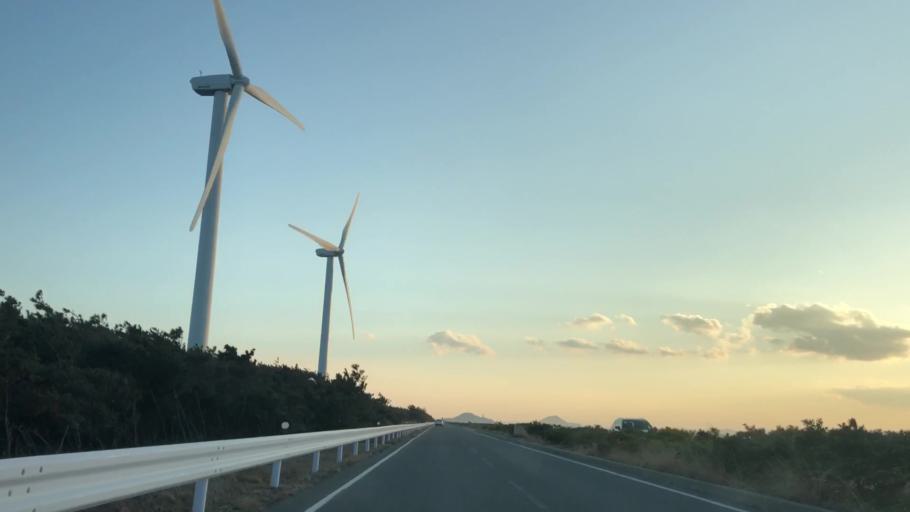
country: JP
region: Aichi
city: Toyohama
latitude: 34.6392
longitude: 137.0529
